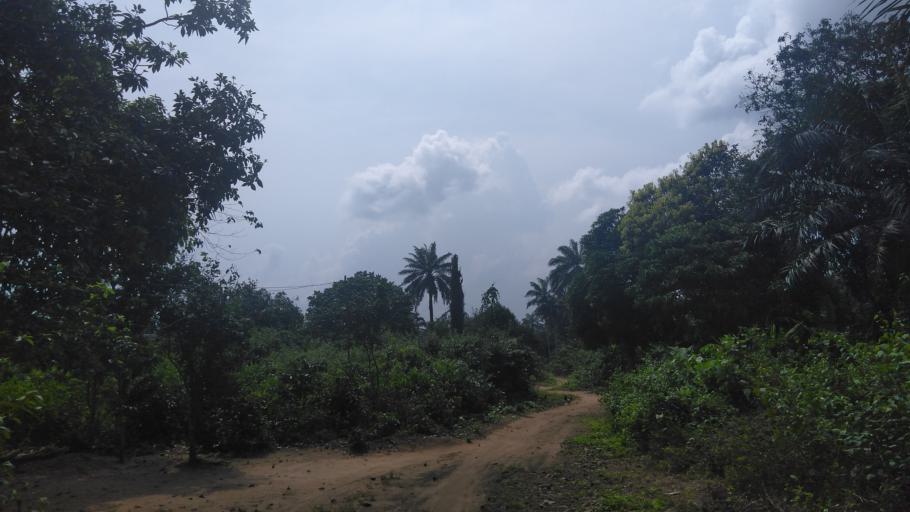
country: NG
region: Abia
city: Aba
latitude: 5.0447
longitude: 7.2393
